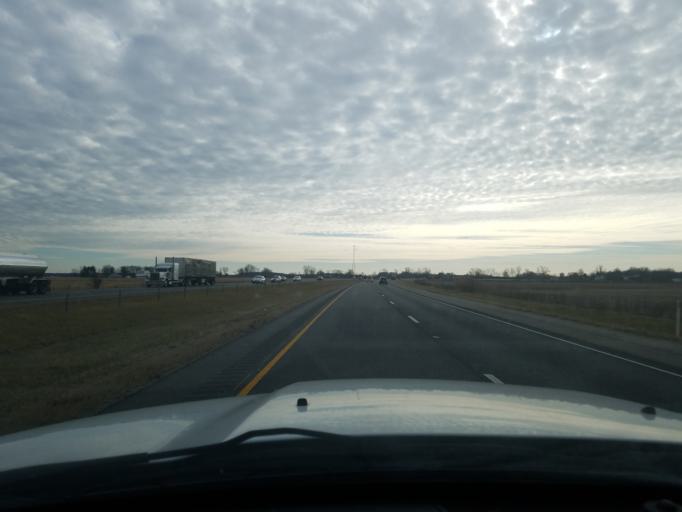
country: US
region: Indiana
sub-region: Delaware County
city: Daleville
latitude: 40.1889
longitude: -85.5612
